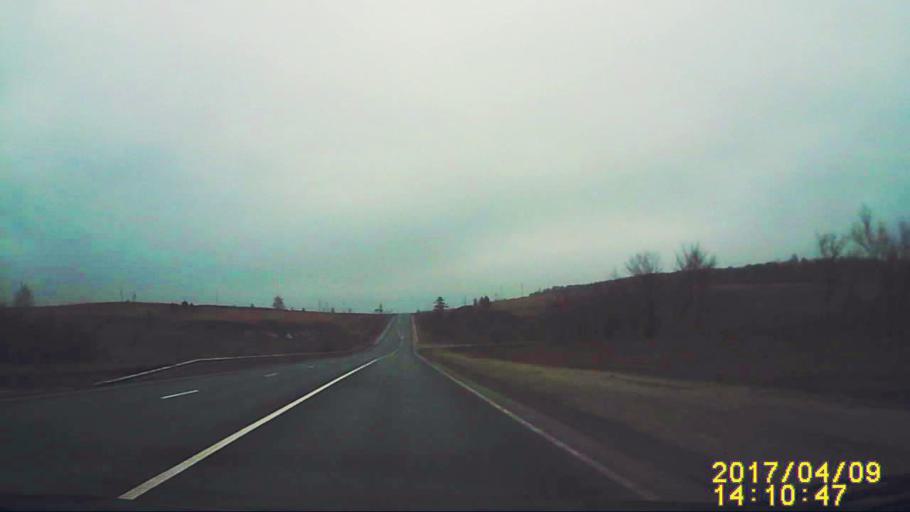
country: RU
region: Ulyanovsk
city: Krasnyy Gulyay
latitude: 54.0415
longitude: 48.2142
